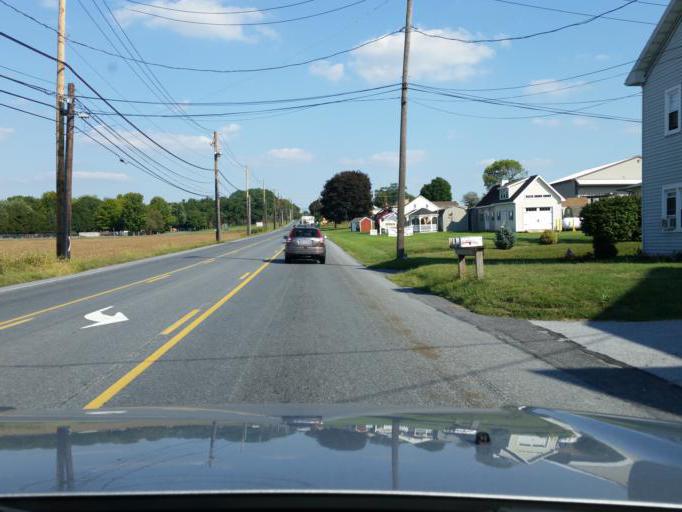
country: US
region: Pennsylvania
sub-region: Lancaster County
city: Gap
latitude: 39.9980
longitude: -76.0582
